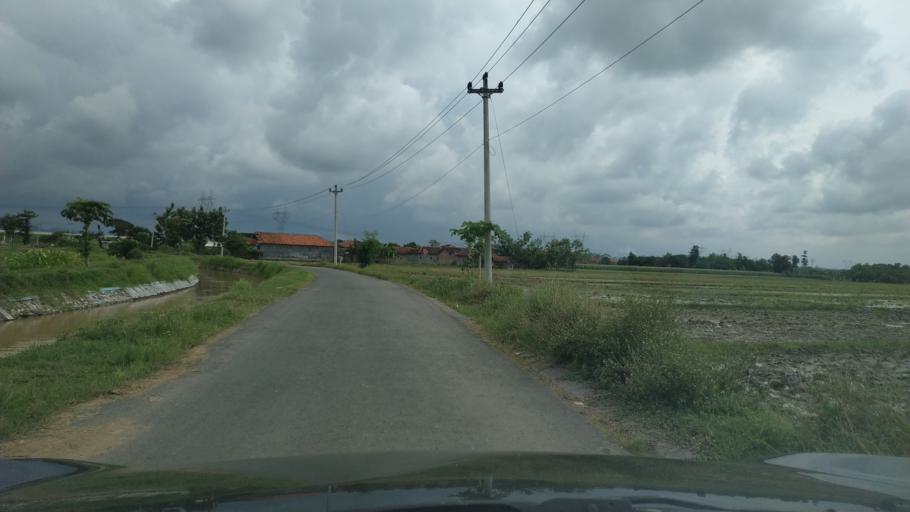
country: ID
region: Central Java
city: Pemalang
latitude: -6.9328
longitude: 109.3371
